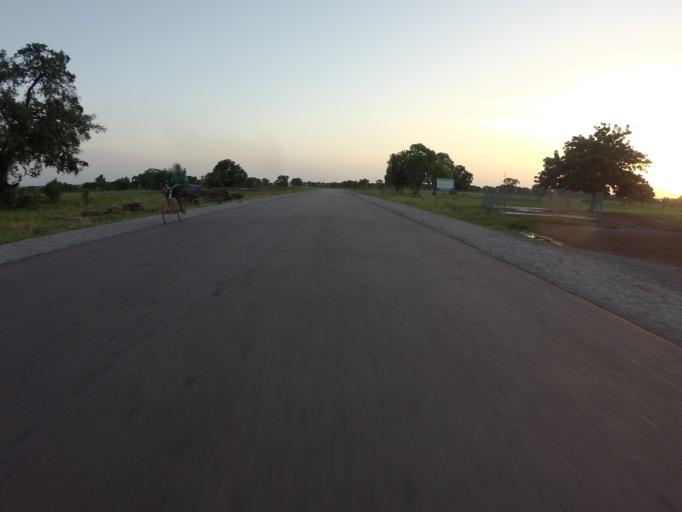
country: GH
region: Northern
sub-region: Yendi
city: Yendi
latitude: 9.9622
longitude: -0.1423
